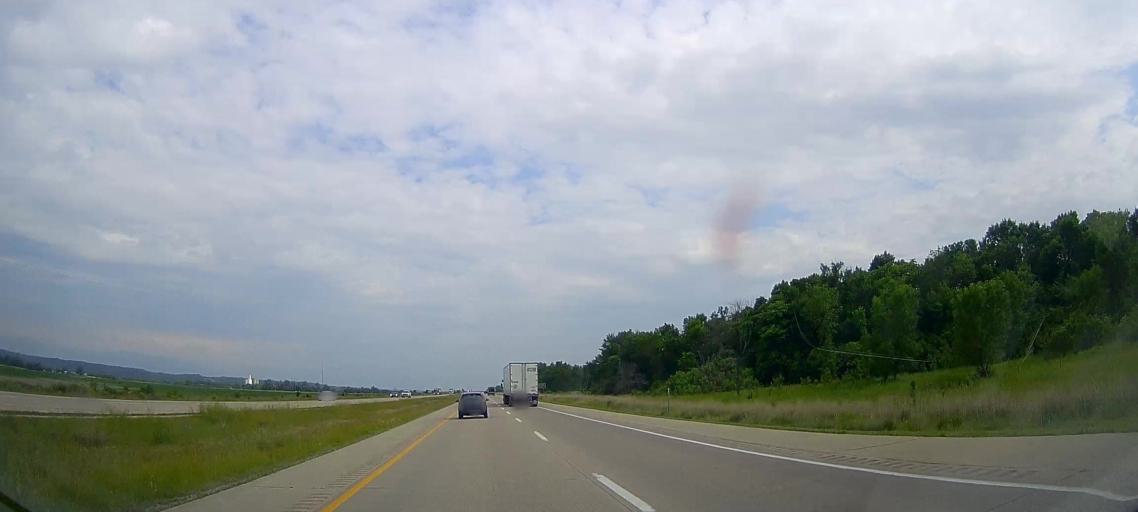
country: US
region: Nebraska
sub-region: Burt County
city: Tekamah
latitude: 41.8155
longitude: -96.0680
